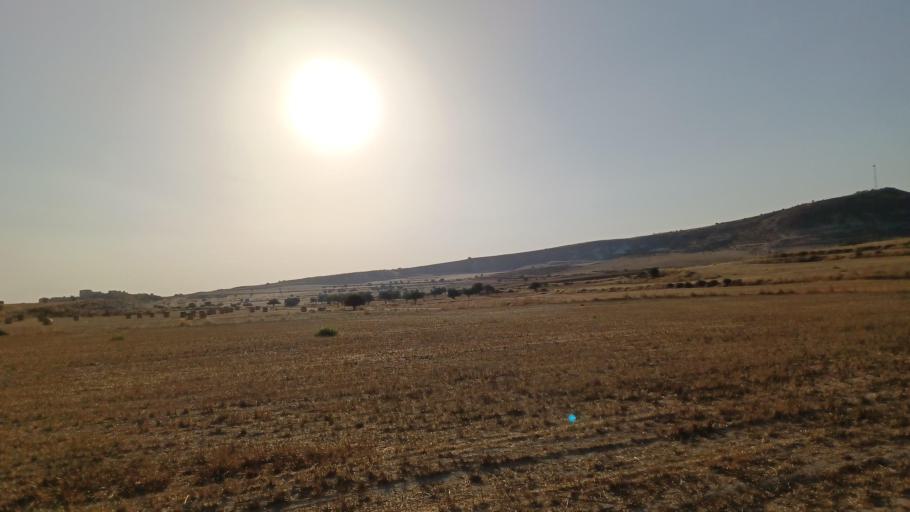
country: CY
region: Larnaka
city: Athienou
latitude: 35.0408
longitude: 33.5117
